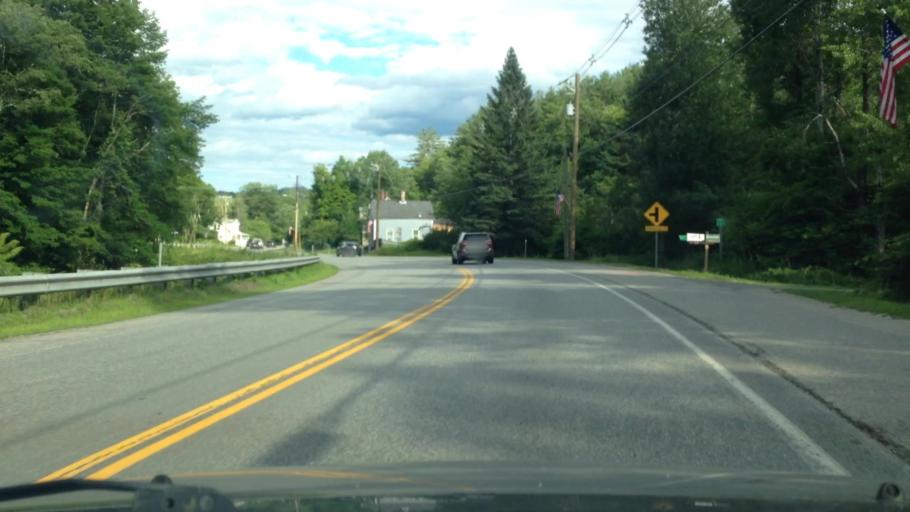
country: US
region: New Hampshire
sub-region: Cheshire County
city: Marlborough
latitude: 42.9106
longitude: -72.2210
